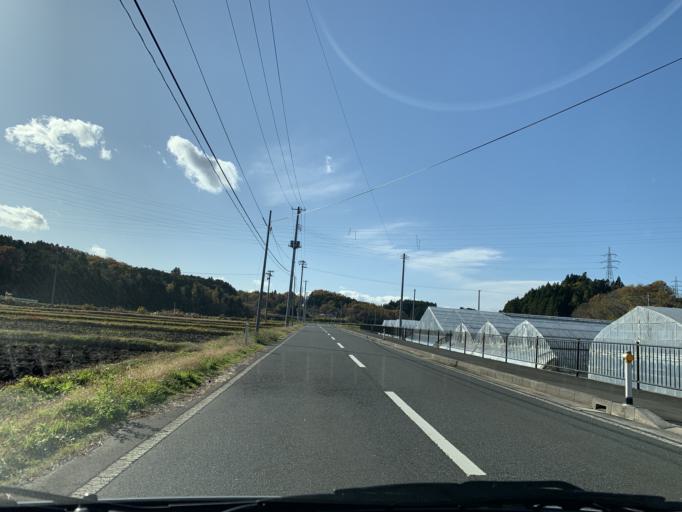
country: JP
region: Iwate
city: Mizusawa
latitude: 39.0924
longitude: 141.1264
